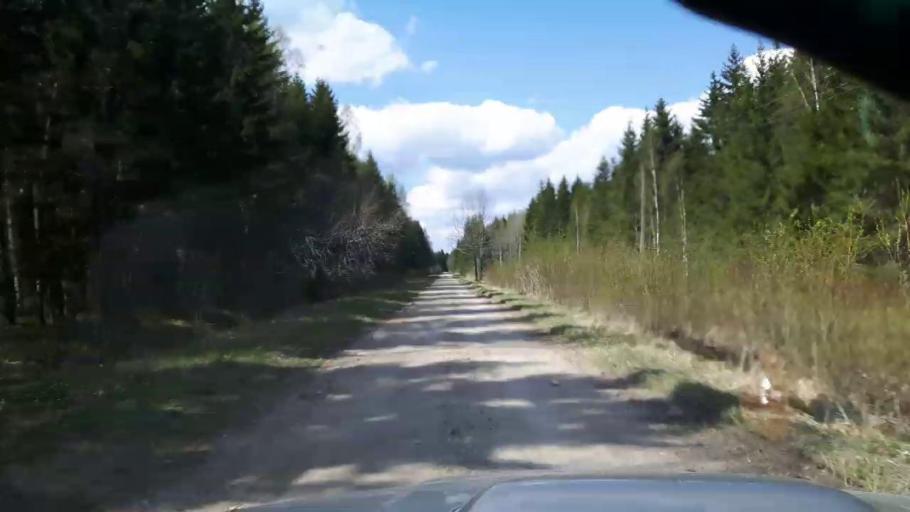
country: EE
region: Paernumaa
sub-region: Tootsi vald
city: Tootsi
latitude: 58.4450
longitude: 24.9130
